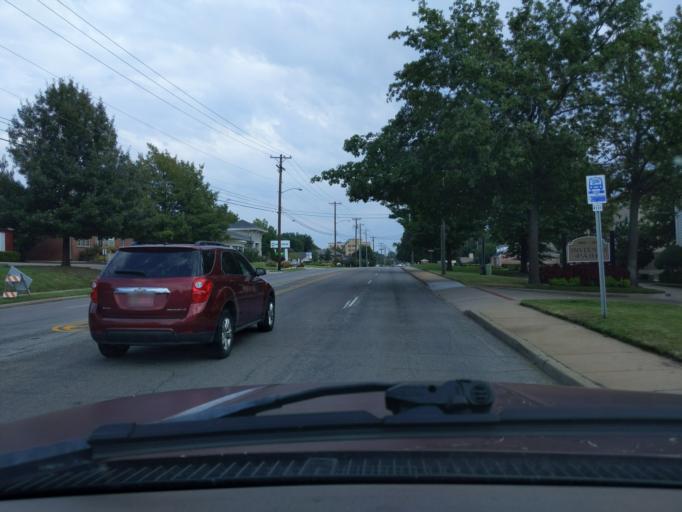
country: US
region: Oklahoma
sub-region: Tulsa County
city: Tulsa
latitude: 36.1333
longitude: -95.9561
